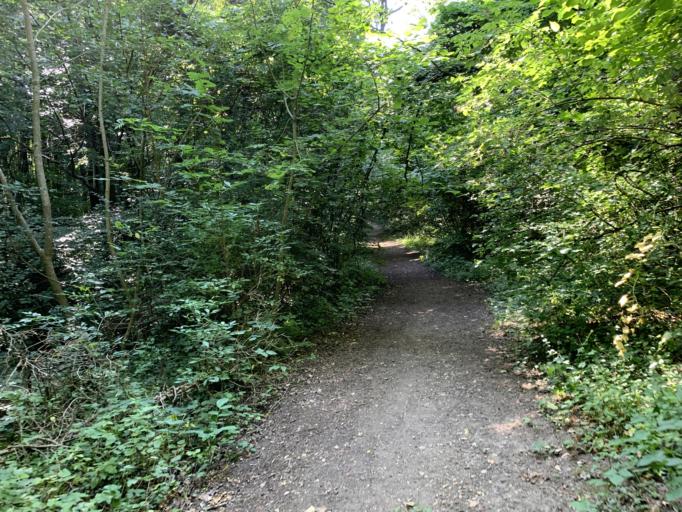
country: CH
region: Vaud
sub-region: Nyon District
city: Genolier
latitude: 46.4325
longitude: 6.2232
